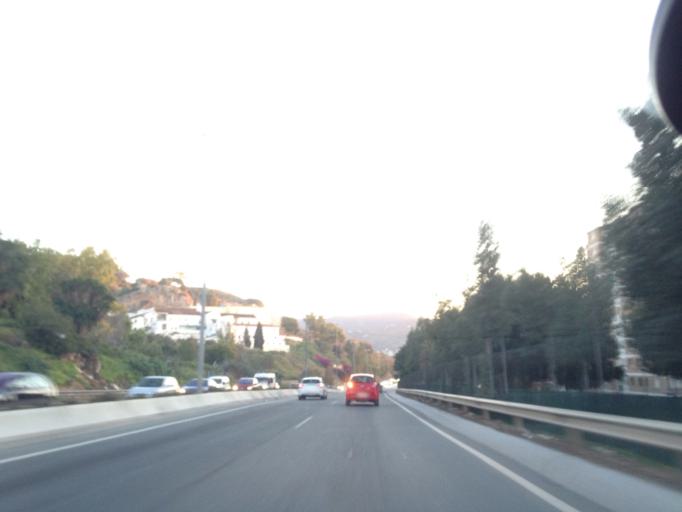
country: ES
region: Andalusia
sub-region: Provincia de Malaga
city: Malaga
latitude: 36.7306
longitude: -4.4425
